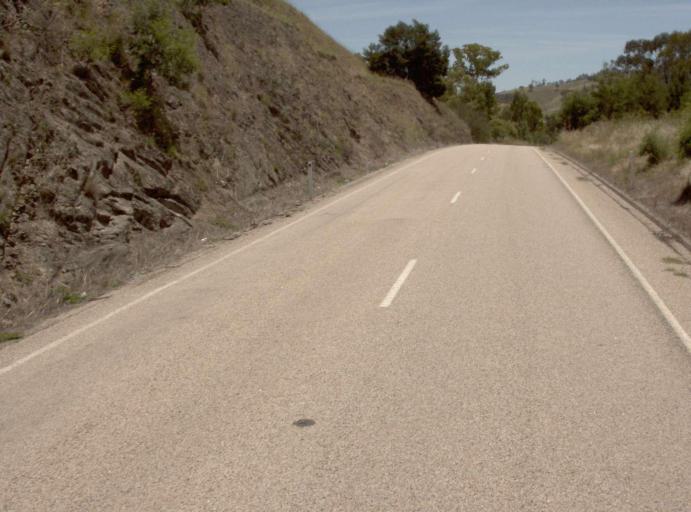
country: AU
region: Victoria
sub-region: East Gippsland
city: Bairnsdale
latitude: -37.5068
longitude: 147.8403
